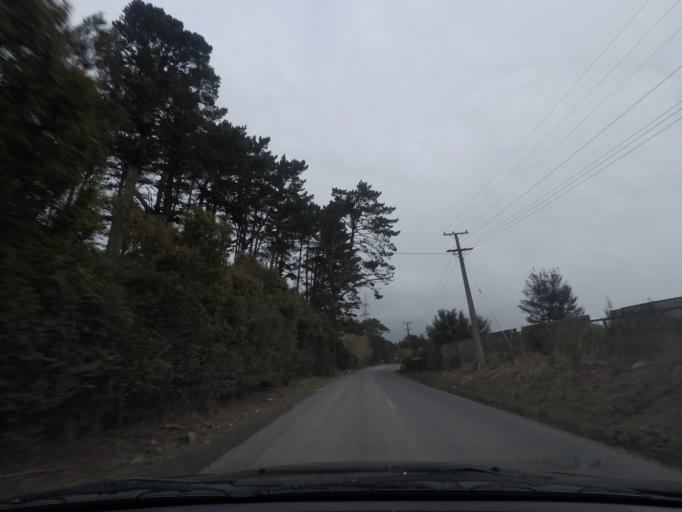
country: NZ
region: Auckland
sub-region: Auckland
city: Muriwai Beach
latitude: -36.7594
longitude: 174.5755
